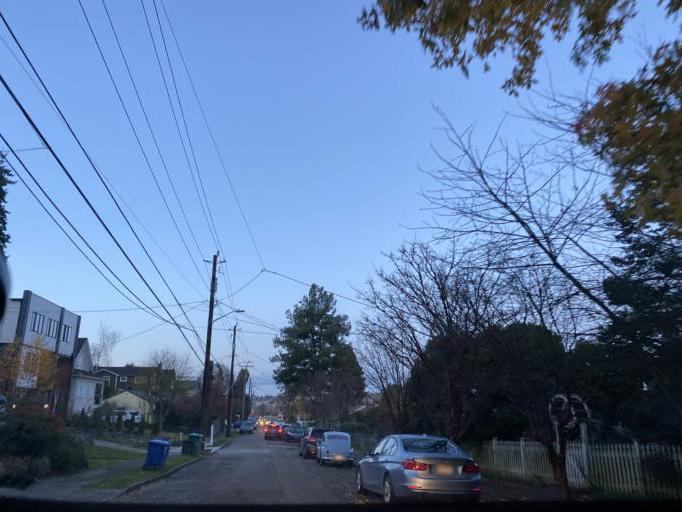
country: US
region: Washington
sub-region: King County
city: Seattle
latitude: 47.6526
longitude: -122.3860
